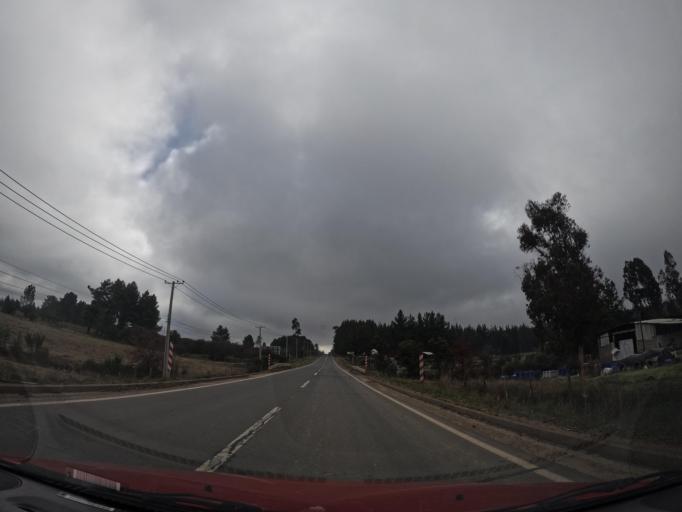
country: CL
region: Maule
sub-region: Provincia de Cauquenes
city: Cauquenes
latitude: -36.2598
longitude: -72.5481
